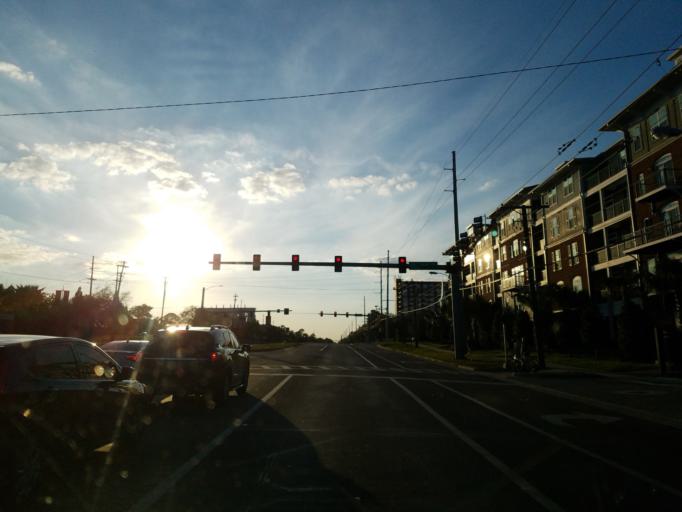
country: US
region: Florida
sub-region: Hillsborough County
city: University
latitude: 28.0692
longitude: -82.4128
